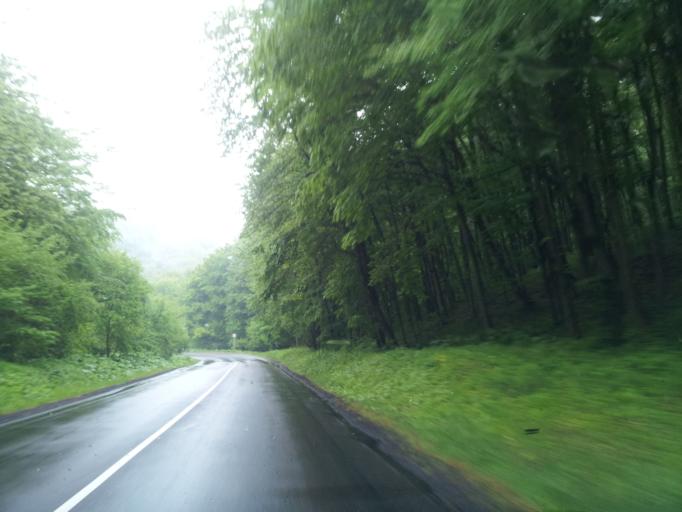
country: HU
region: Baranya
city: Komlo
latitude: 46.2134
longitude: 18.3006
